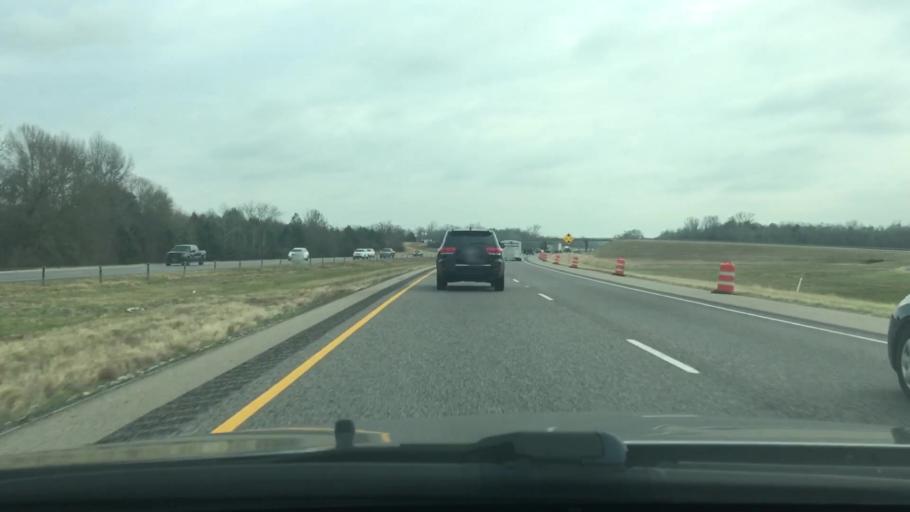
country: US
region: Texas
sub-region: Leon County
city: Buffalo
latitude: 31.5037
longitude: -96.0988
